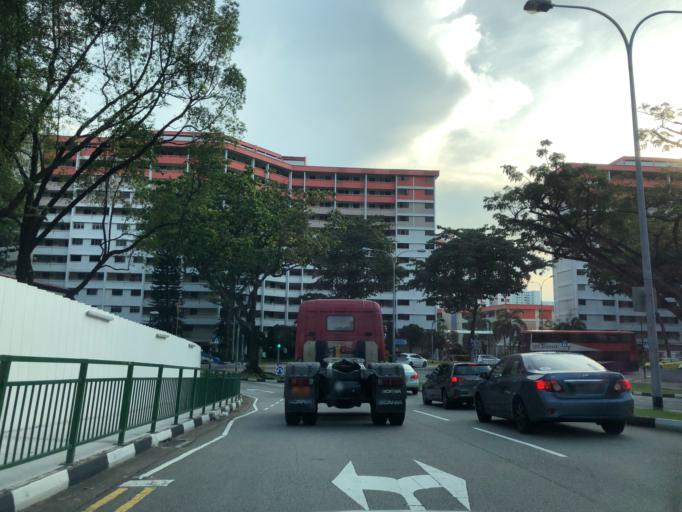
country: SG
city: Singapore
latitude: 1.2783
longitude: 103.8320
